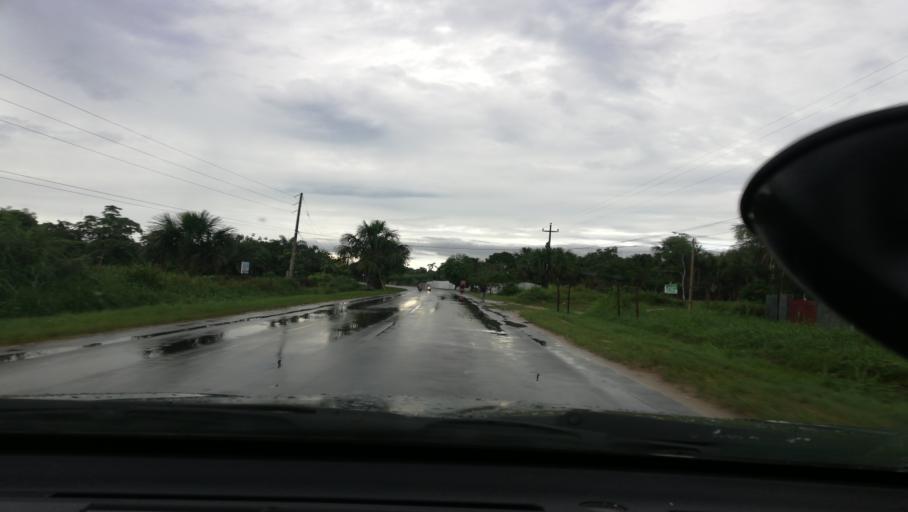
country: PE
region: Loreto
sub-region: Provincia de Maynas
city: Iquitos
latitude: -3.8495
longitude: -73.3384
